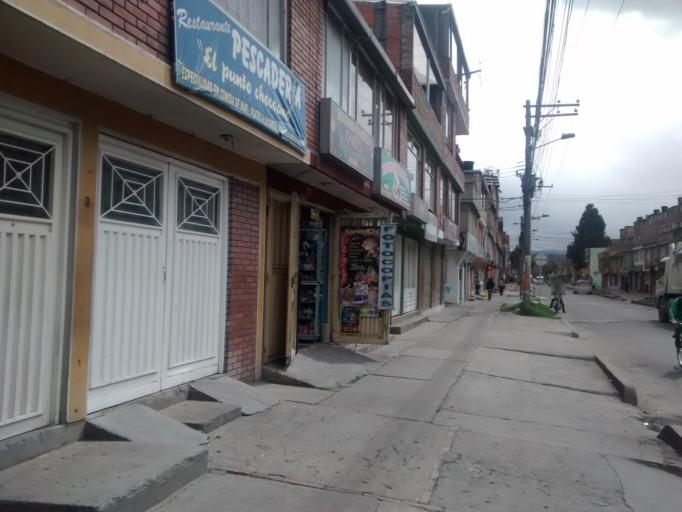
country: CO
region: Cundinamarca
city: Cota
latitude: 4.7150
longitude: -74.1058
